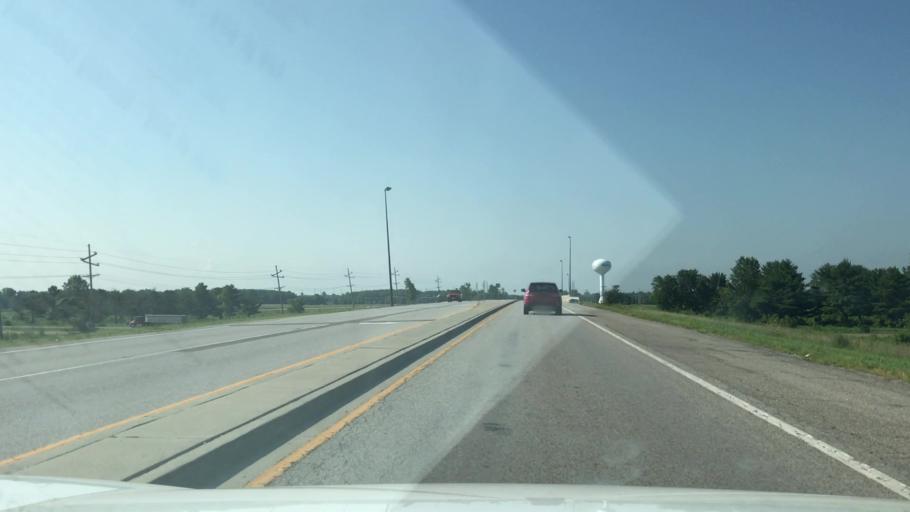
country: US
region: Illinois
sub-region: Saint Clair County
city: Scott Air Force Base
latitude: 38.5532
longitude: -89.8071
